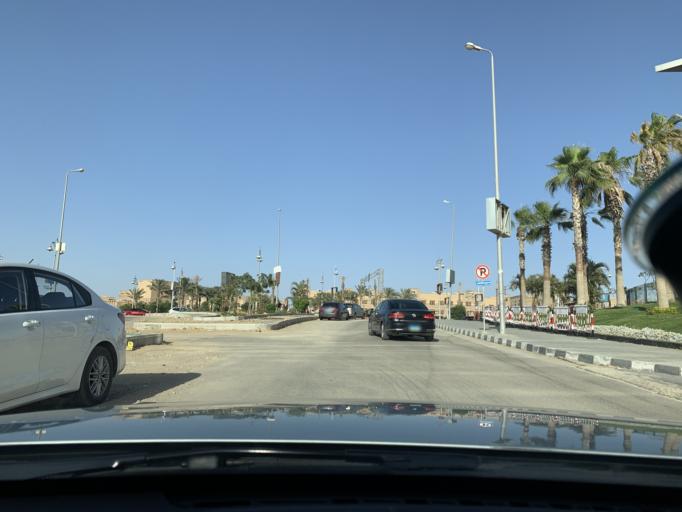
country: EG
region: Muhafazat al Qalyubiyah
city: Al Khankah
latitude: 30.0213
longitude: 31.4948
